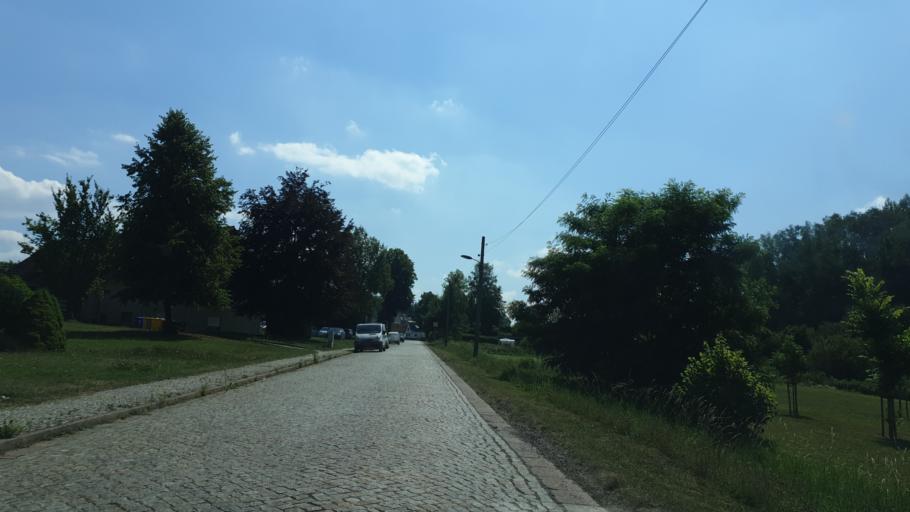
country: DE
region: Saxony
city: Gersdorf
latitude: 50.7490
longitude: 12.7113
